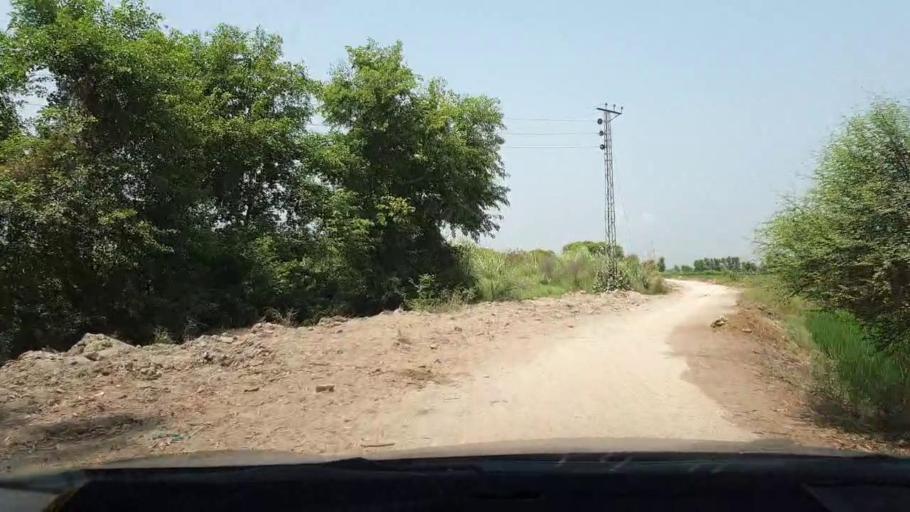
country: PK
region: Sindh
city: Naudero
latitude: 27.6640
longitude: 68.3144
